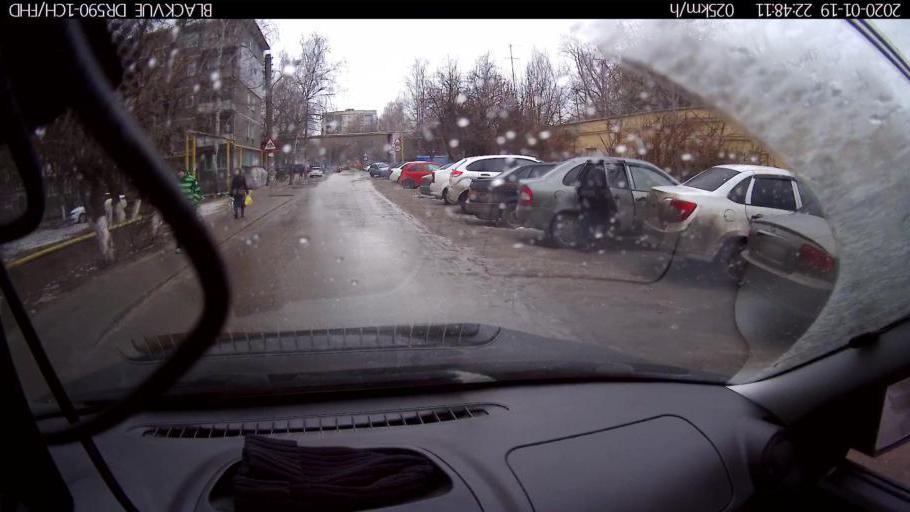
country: RU
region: Nizjnij Novgorod
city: Nizhniy Novgorod
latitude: 56.2823
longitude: 43.9214
